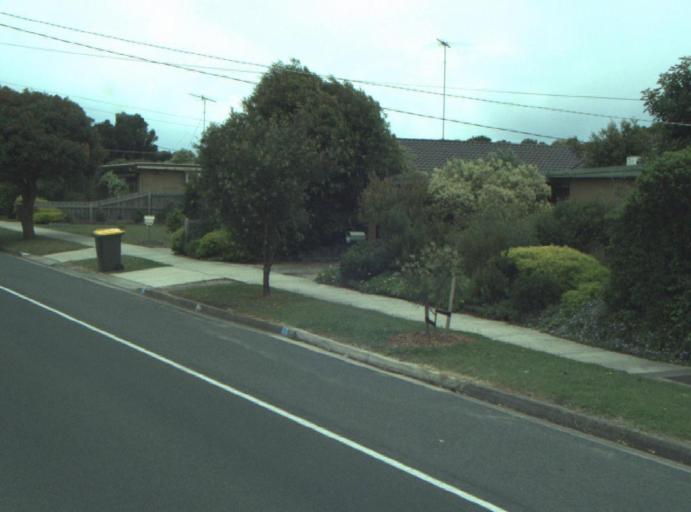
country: AU
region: Victoria
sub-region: Greater Geelong
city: Leopold
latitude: -38.1895
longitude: 144.4739
